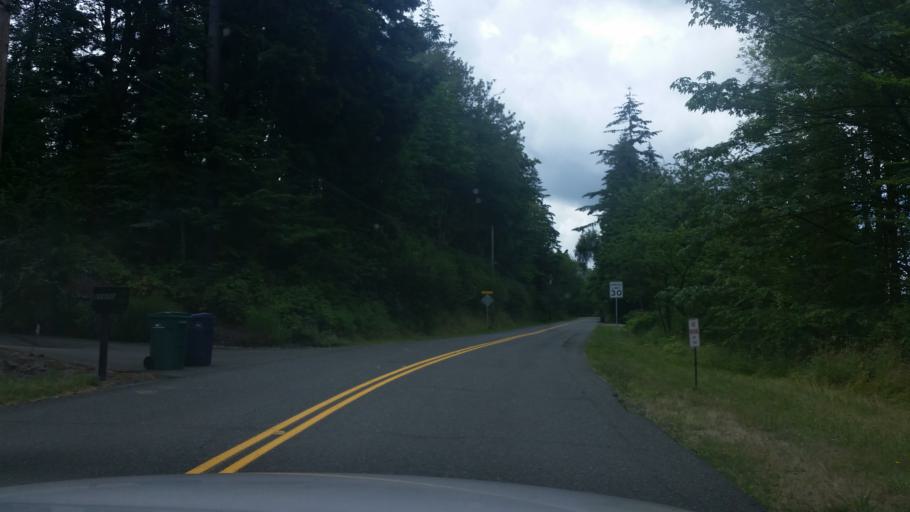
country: US
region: Washington
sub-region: King County
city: Redmond
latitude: 47.7044
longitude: -122.1337
